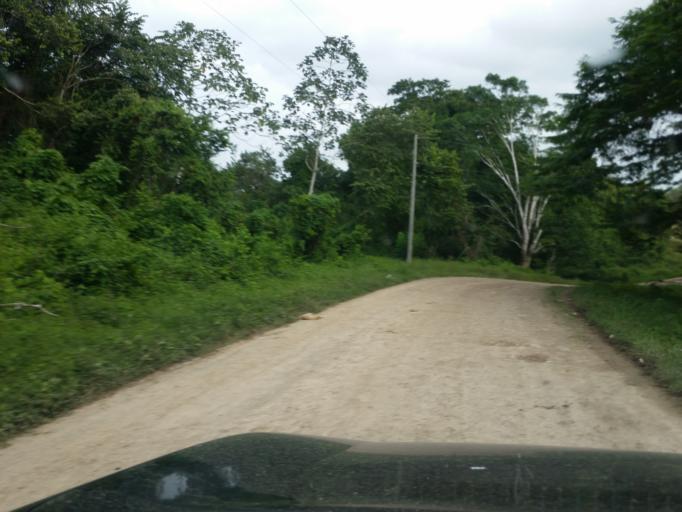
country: CR
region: Alajuela
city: Los Chiles
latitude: 11.1204
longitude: -84.6019
